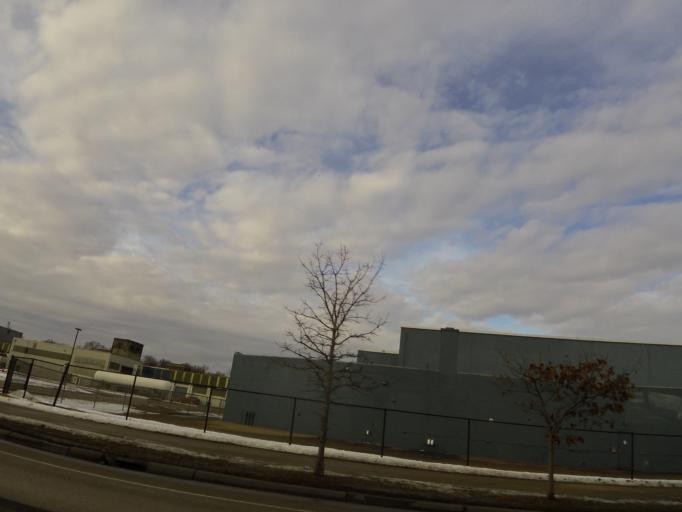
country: US
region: Minnesota
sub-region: Ramsey County
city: Saint Paul
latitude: 44.9657
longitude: -93.0625
